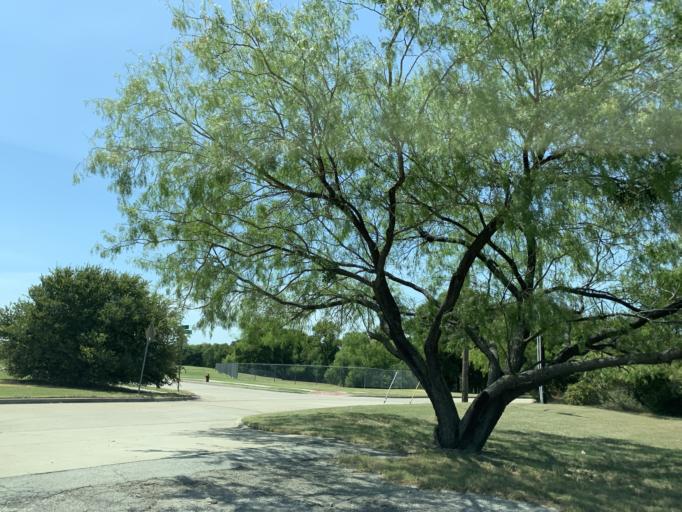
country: US
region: Texas
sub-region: Dallas County
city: Cedar Hill
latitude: 32.6418
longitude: -97.0134
